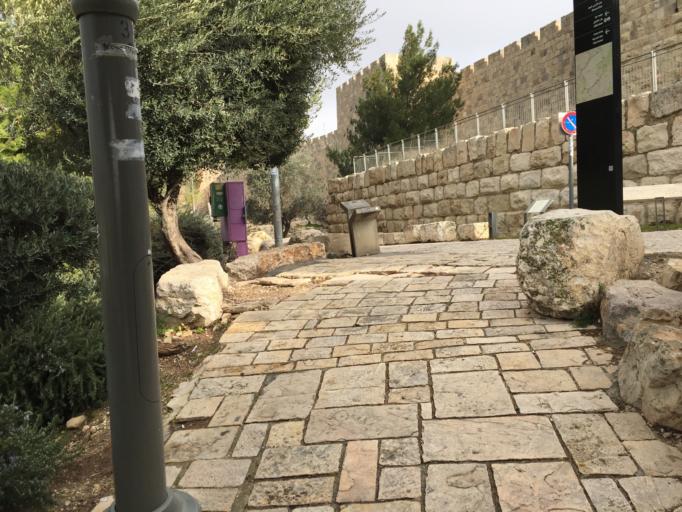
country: PS
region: West Bank
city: Old City
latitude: 31.7728
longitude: 35.2274
